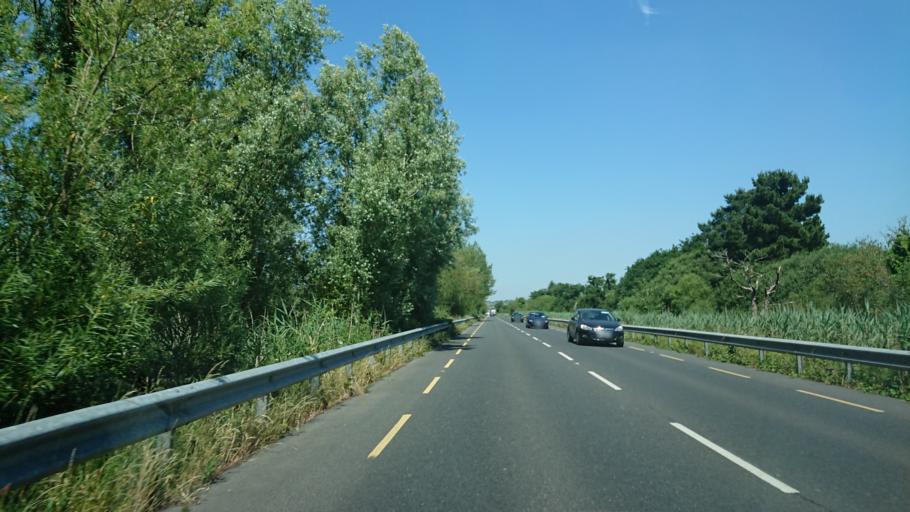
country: IE
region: Munster
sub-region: Waterford
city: Waterford
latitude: 52.2367
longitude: -7.1208
